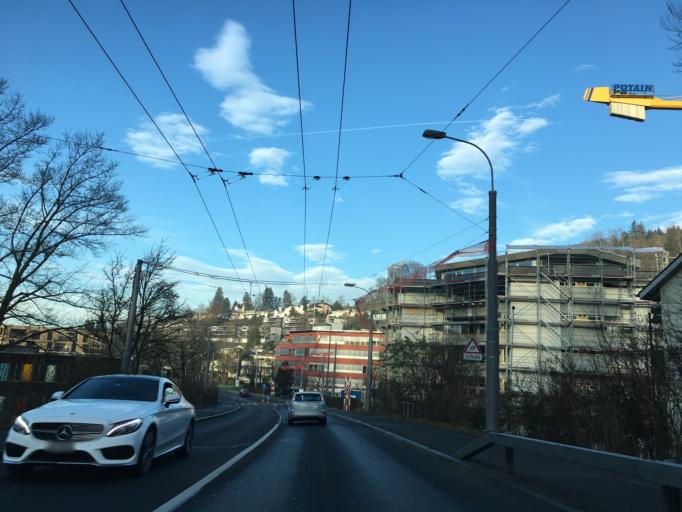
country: CH
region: Lucerne
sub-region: Lucerne-Land District
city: Adligenswil
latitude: 47.0538
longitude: 8.3443
